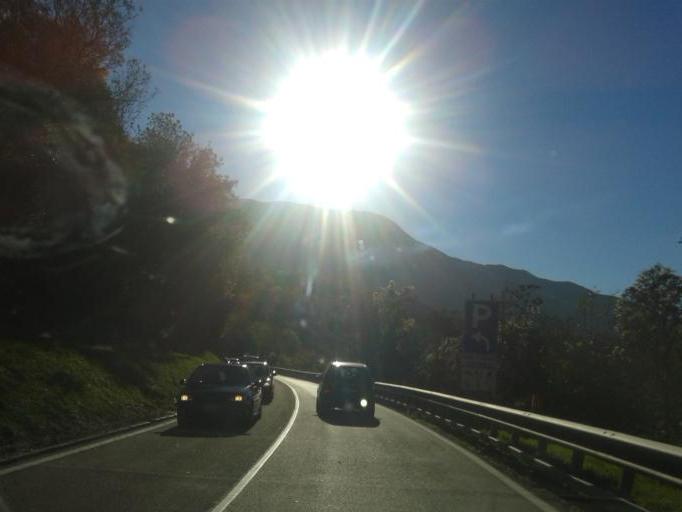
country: IT
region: Trentino-Alto Adige
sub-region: Provincia di Trento
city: Terlago
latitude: 46.0837
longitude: 11.0497
